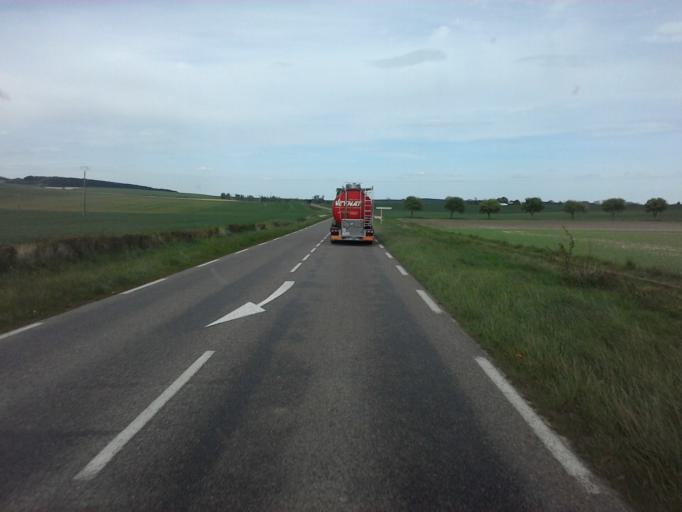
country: FR
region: Champagne-Ardenne
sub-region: Departement de l'Aube
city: Bouilly
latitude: 48.1382
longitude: 4.0002
